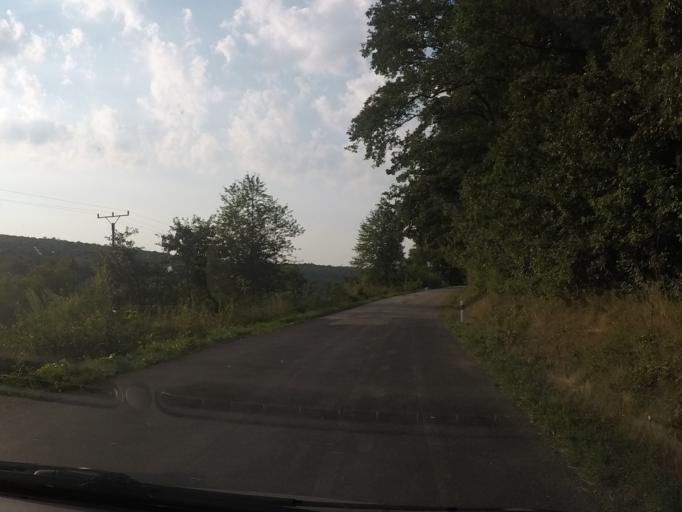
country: SK
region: Nitriansky
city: Zlate Moravce
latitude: 48.4508
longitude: 18.3255
